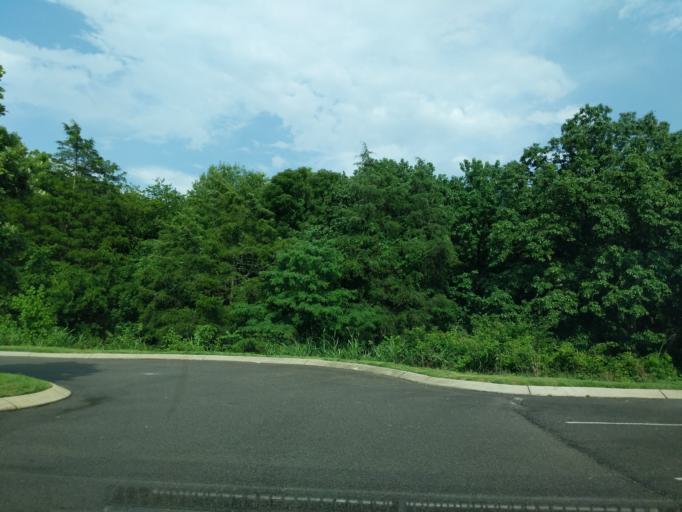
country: US
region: Tennessee
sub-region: Davidson County
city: Belle Meade
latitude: 36.0424
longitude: -86.9526
